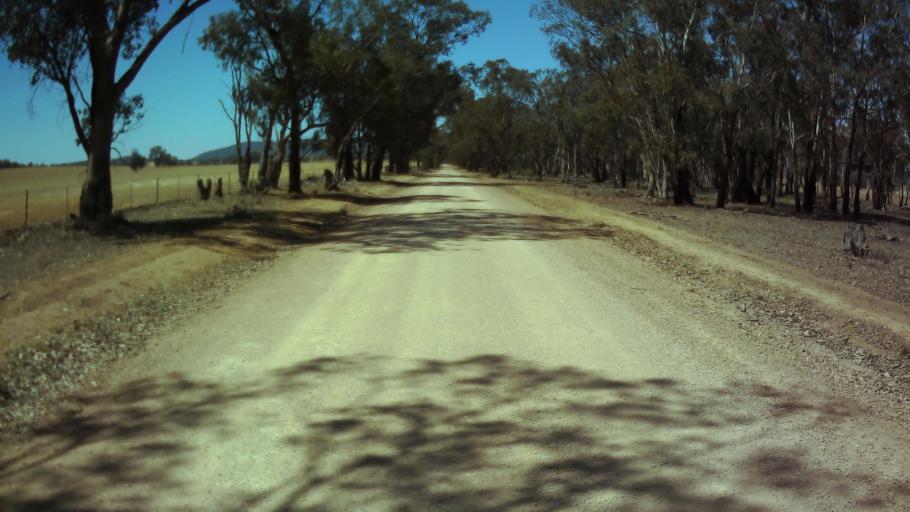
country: AU
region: New South Wales
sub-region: Weddin
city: Grenfell
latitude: -33.9116
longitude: 148.0798
